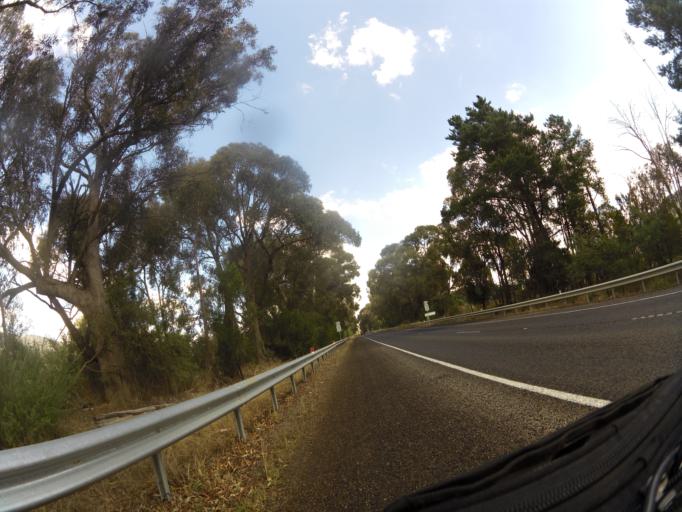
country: AU
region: Victoria
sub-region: Mansfield
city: Mansfield
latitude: -36.8310
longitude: 146.0085
